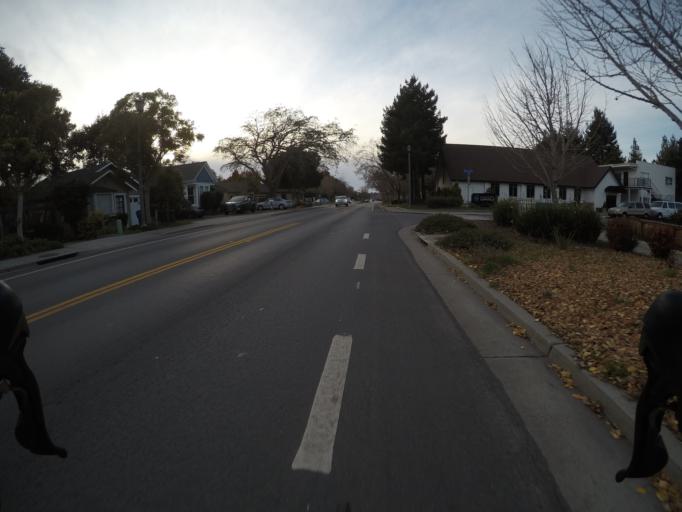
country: US
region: California
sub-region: Santa Cruz County
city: Capitola
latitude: 36.9738
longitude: -121.9589
